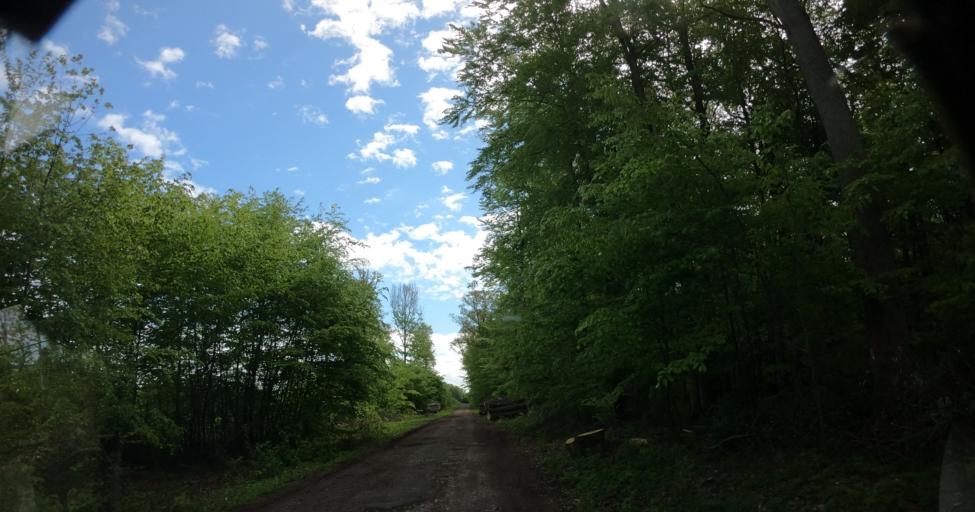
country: PL
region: West Pomeranian Voivodeship
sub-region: Powiat stargardzki
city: Dobrzany
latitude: 53.3474
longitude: 15.4903
